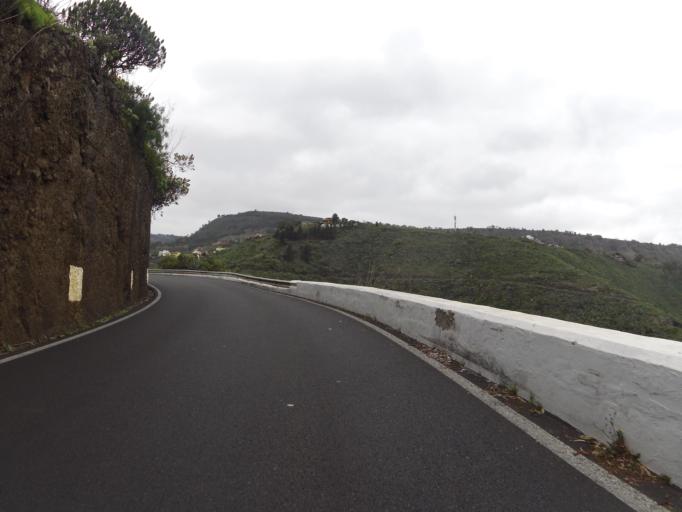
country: ES
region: Canary Islands
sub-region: Provincia de Las Palmas
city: Arucas
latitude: 28.0821
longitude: -15.5133
